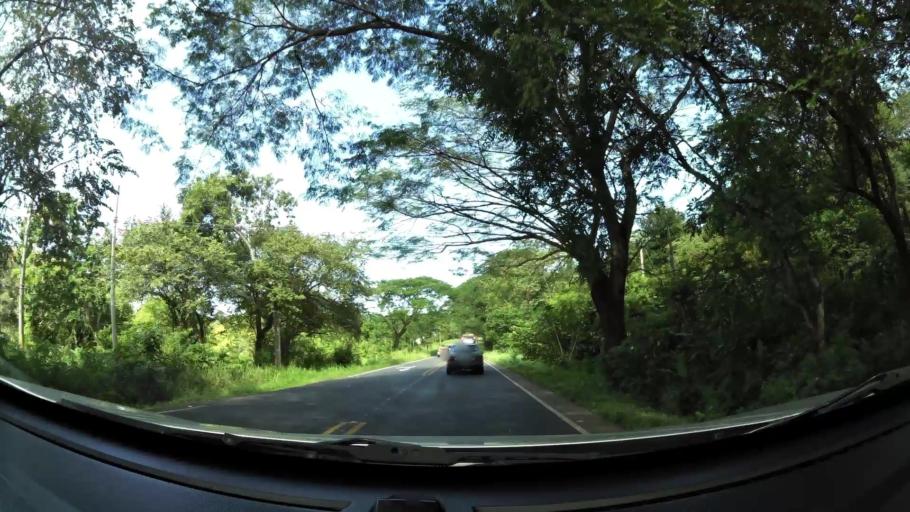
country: CR
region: Guanacaste
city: Juntas
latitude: 10.3112
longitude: -85.0416
